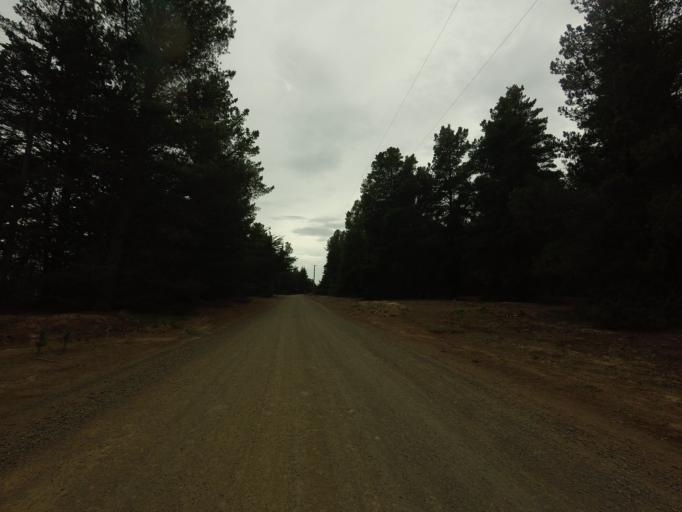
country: AU
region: Tasmania
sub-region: Clarence
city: Seven Mile Beach
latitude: -42.8346
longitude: 147.5345
